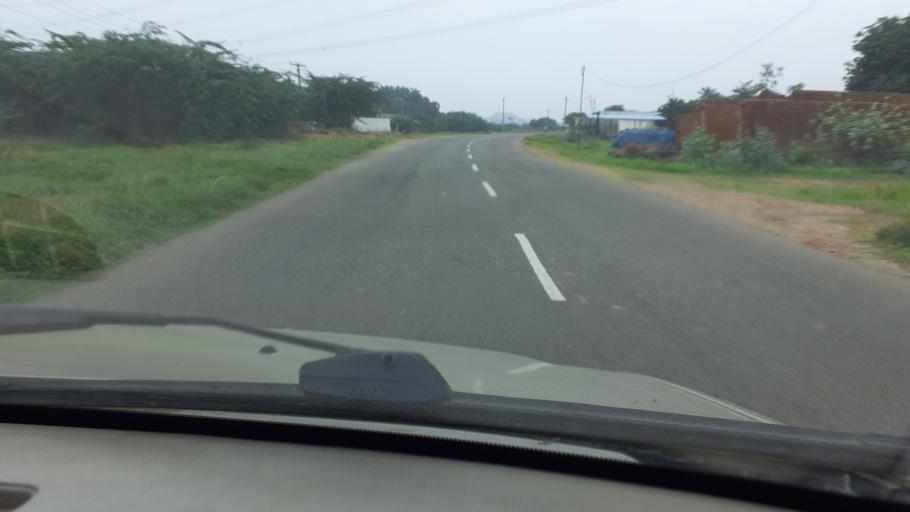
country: IN
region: Tamil Nadu
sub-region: Tirunelveli Kattabo
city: Nanguneri
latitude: 8.4867
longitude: 77.6465
